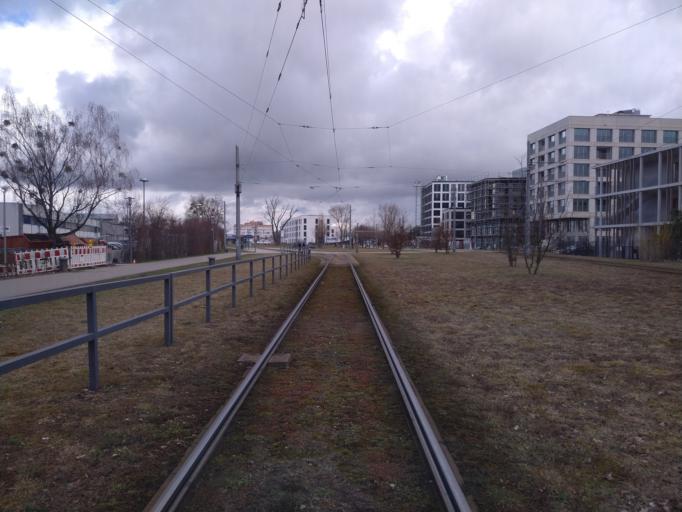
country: DE
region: Bavaria
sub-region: Upper Bavaria
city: Bogenhausen
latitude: 48.1857
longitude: 11.5907
